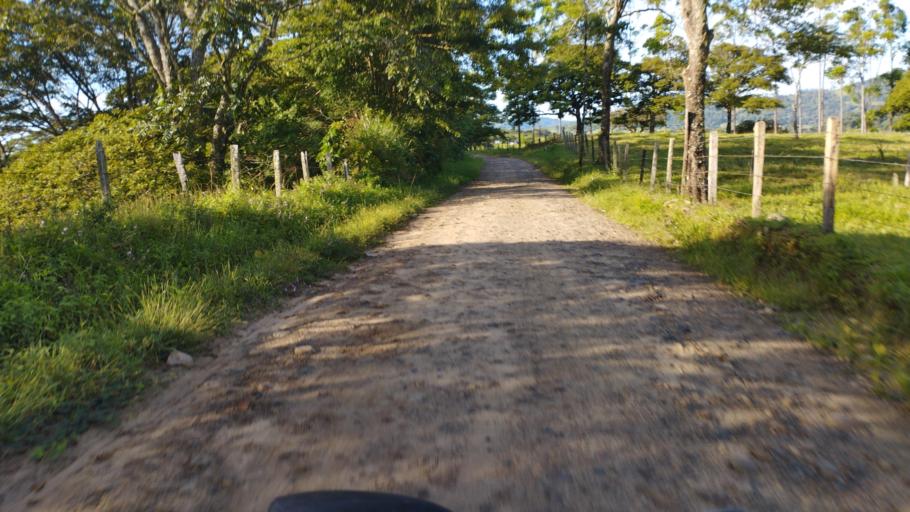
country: CO
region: Casanare
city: Sabanalarga
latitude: 4.8001
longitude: -73.0917
